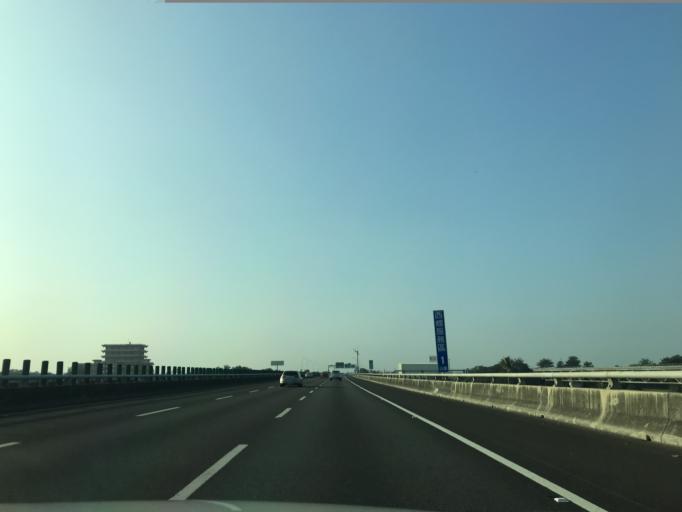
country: TW
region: Taiwan
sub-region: Yunlin
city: Douliu
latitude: 23.7998
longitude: 120.4822
